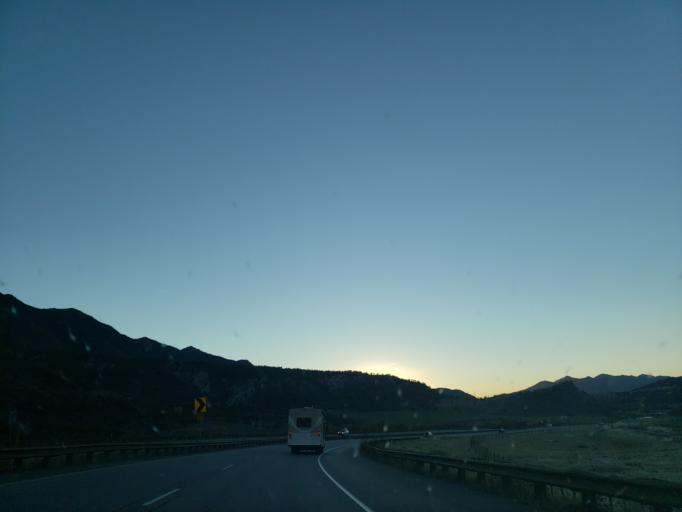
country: US
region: Colorado
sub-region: Garfield County
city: New Castle
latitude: 39.5709
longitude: -107.4568
